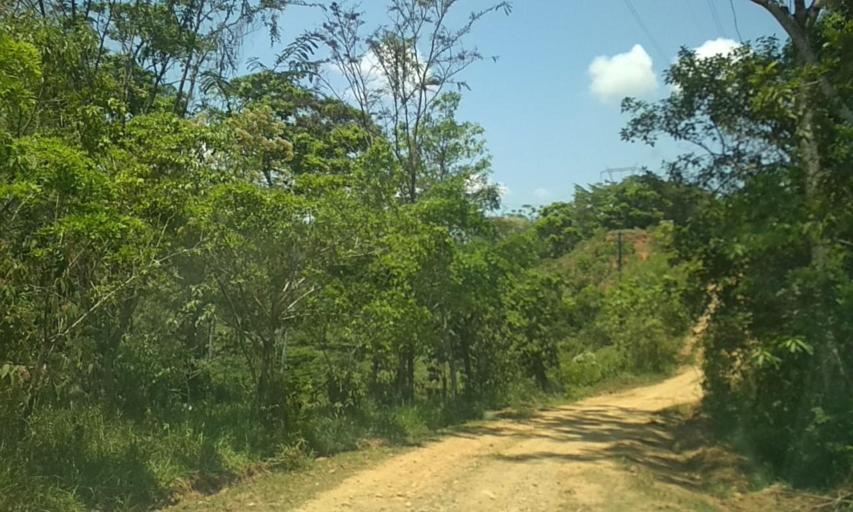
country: MX
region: Chiapas
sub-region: Tecpatan
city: Raudales Malpaso
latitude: 17.3930
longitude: -93.7383
